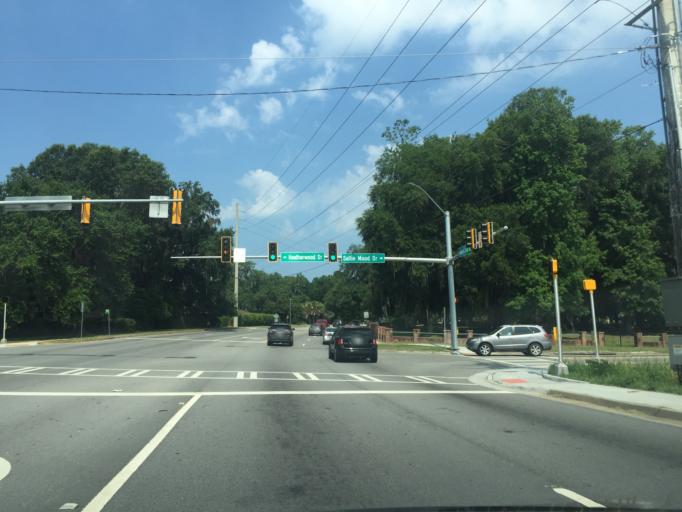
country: US
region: Georgia
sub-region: Chatham County
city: Isle of Hope
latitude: 31.9904
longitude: -81.0902
